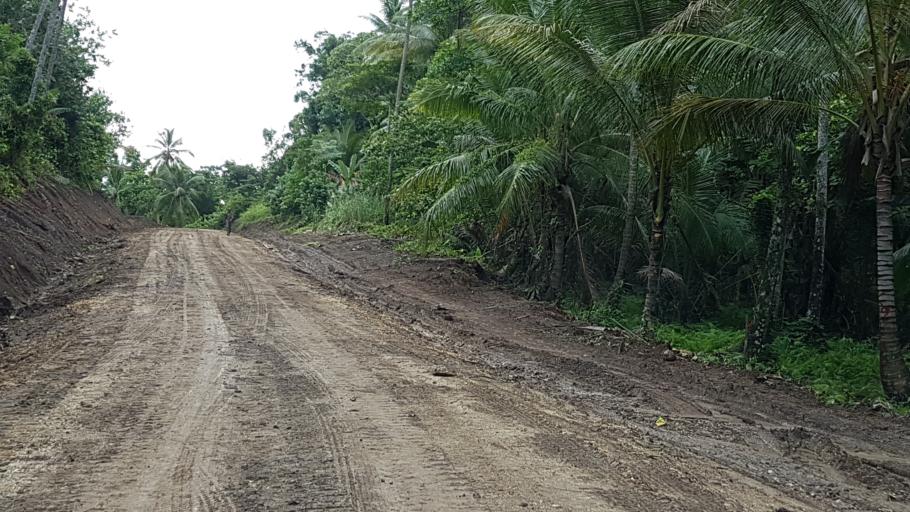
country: PG
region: Milne Bay
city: Alotau
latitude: -10.2984
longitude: 150.7603
